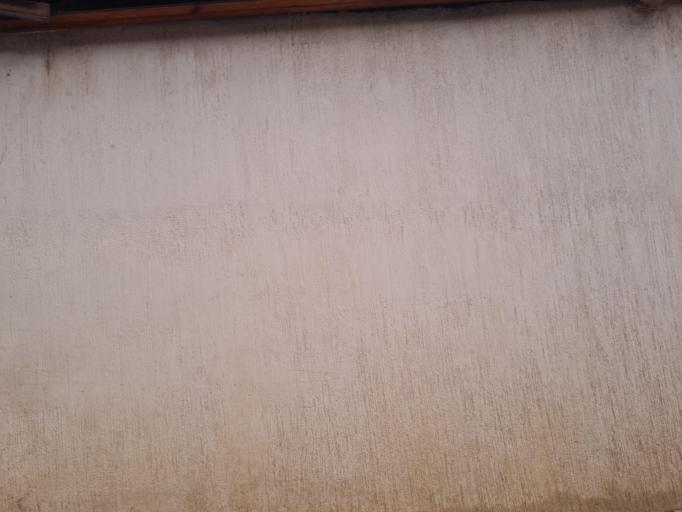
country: GT
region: Quetzaltenango
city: Quetzaltenango
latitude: 14.8373
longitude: -91.5337
